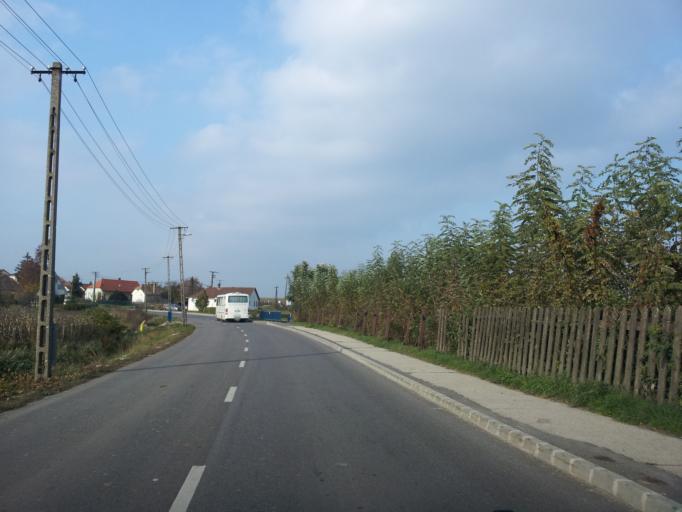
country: HU
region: Komarom-Esztergom
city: Bokod
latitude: 47.4939
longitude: 18.2433
